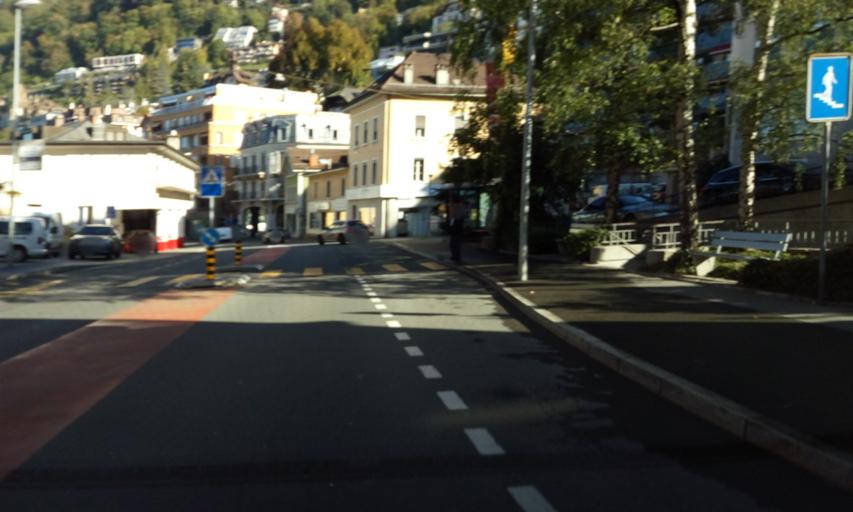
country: CH
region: Vaud
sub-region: Riviera-Pays-d'Enhaut District
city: Caux
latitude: 46.4231
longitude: 6.9255
